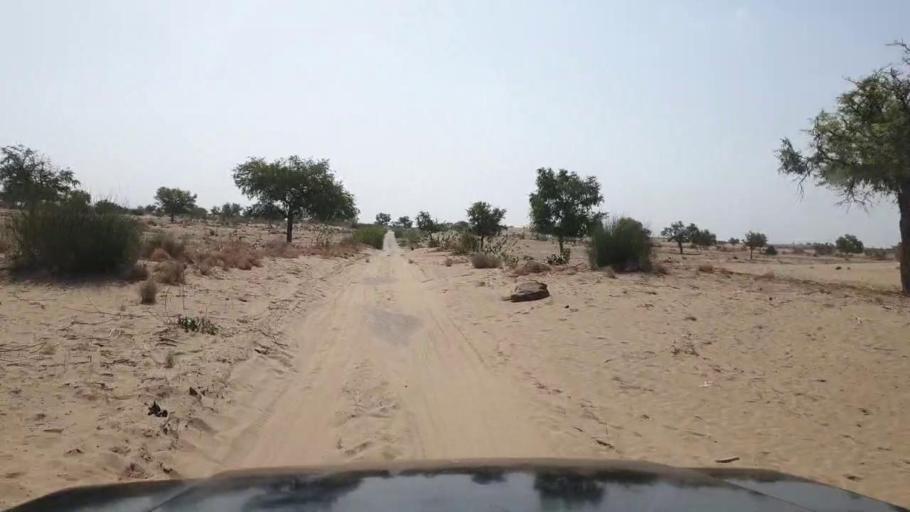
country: PK
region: Sindh
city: Islamkot
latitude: 24.9213
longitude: 70.1376
